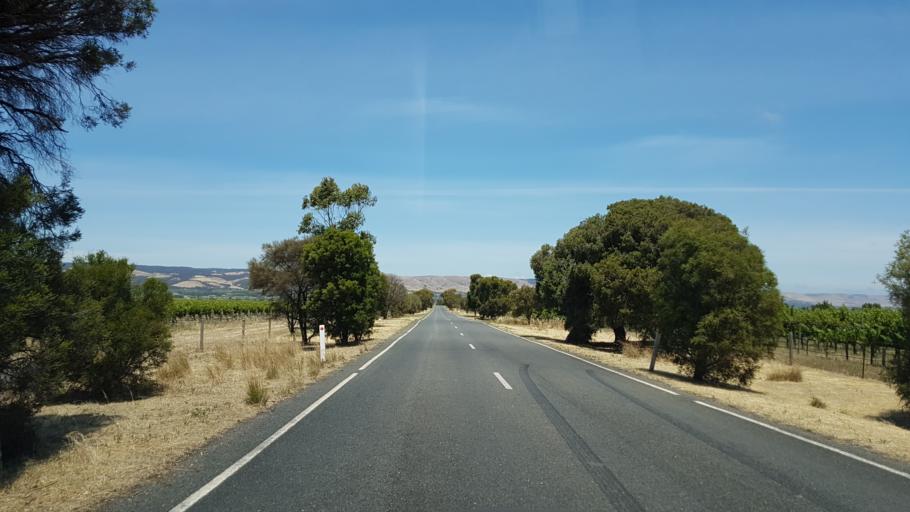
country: AU
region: South Australia
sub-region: Onkaparinga
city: McLaren Vale
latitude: -35.2353
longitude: 138.5193
